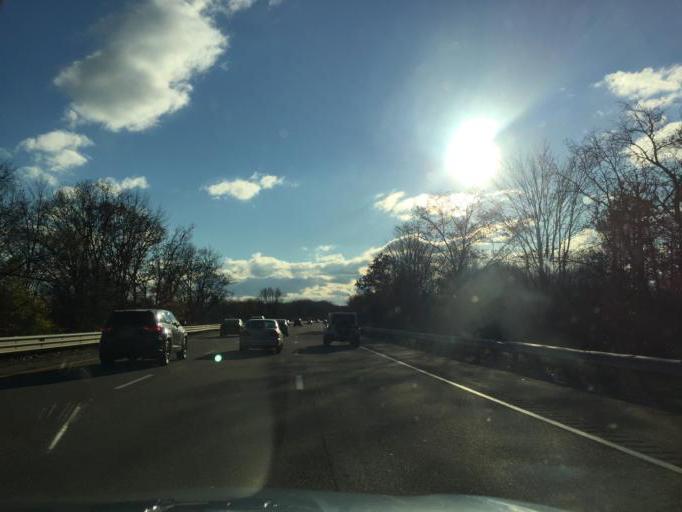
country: US
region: Massachusetts
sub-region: Bristol County
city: North Seekonk
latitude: 41.9124
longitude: -71.3379
